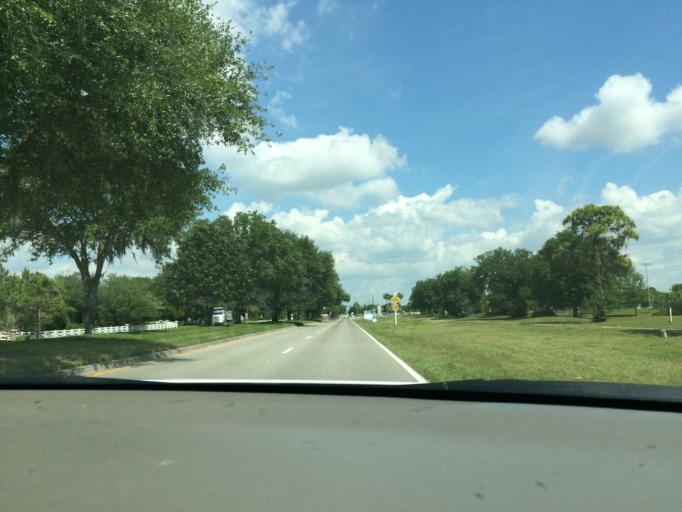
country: US
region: Florida
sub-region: Sarasota County
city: The Meadows
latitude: 27.3864
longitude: -82.4199
